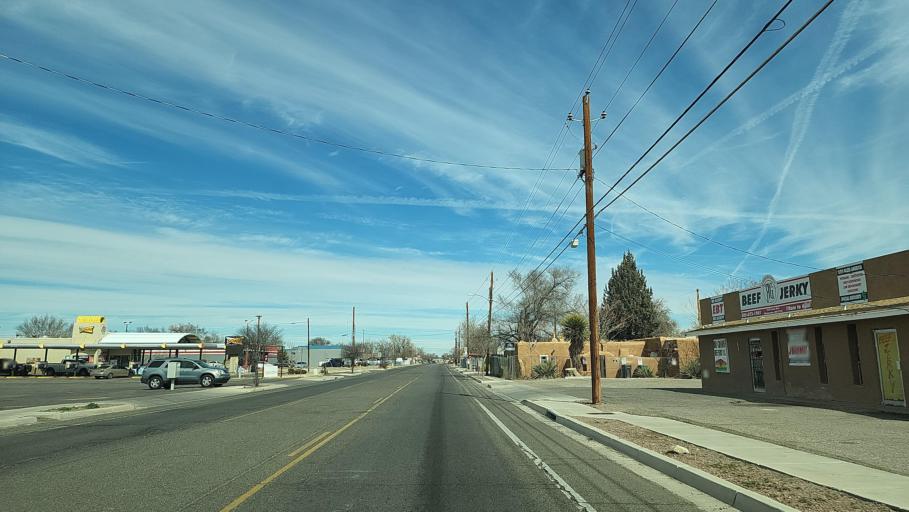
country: US
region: New Mexico
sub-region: Bernalillo County
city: South Valley
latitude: 35.0341
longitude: -106.6794
